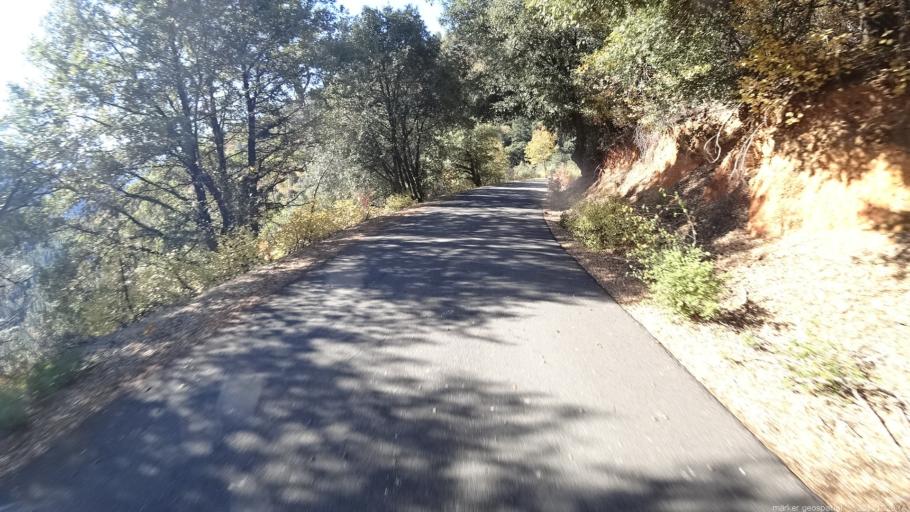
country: US
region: California
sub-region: Trinity County
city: Lewiston
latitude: 40.8029
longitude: -122.6116
